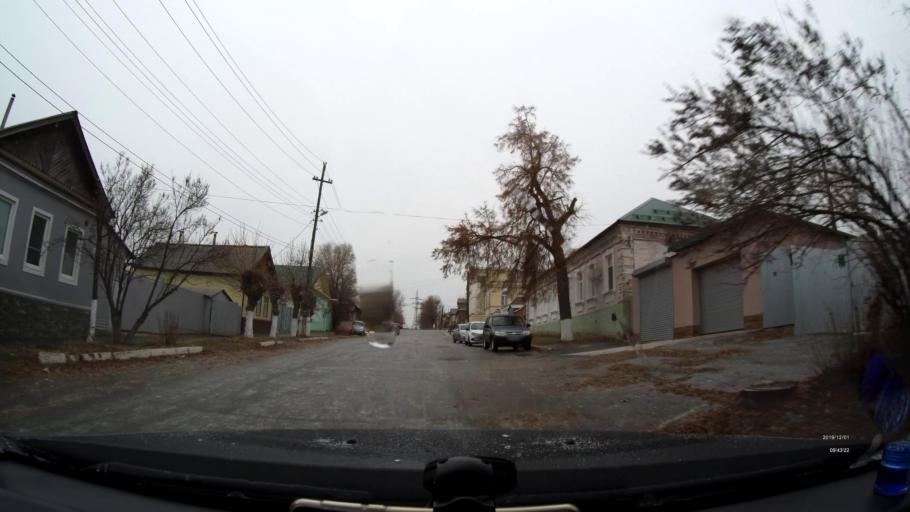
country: RU
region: Saratov
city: Vol'sk
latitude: 52.0434
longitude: 47.3824
